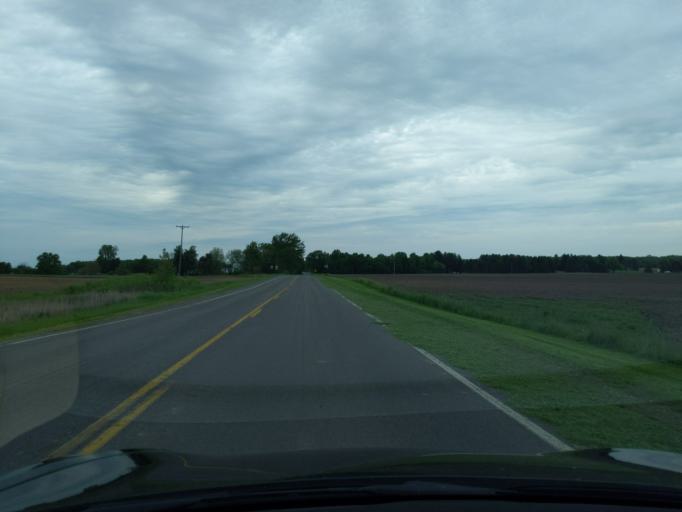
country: US
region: Michigan
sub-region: Ingham County
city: Mason
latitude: 42.5963
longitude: -84.3576
